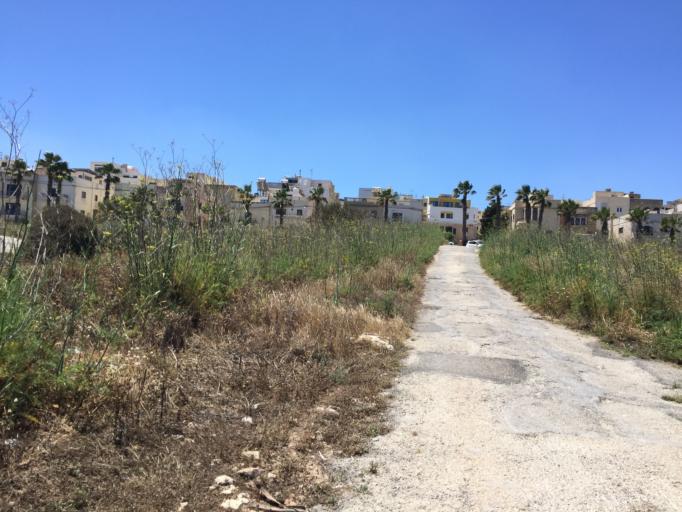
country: MT
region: Pembroke
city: Pembroke
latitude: 35.9295
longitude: 14.4838
